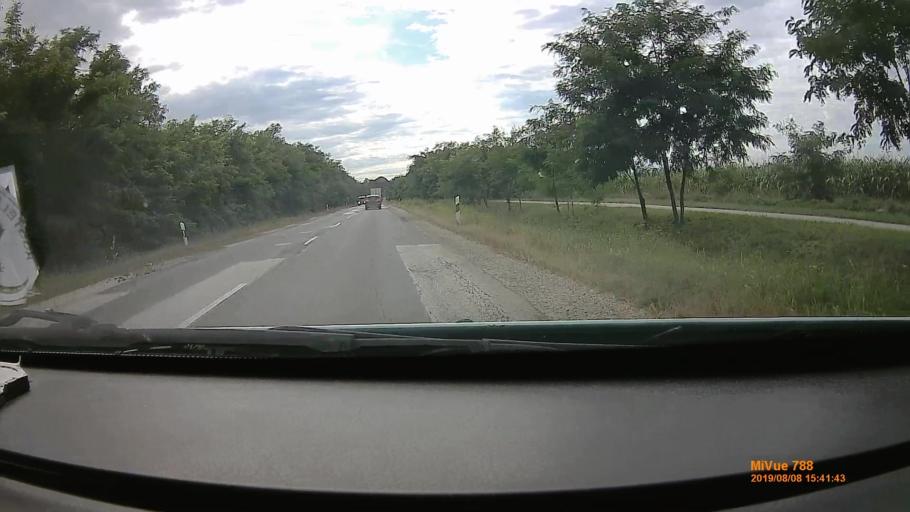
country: HU
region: Szabolcs-Szatmar-Bereg
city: Kocsord
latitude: 47.9384
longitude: 22.4071
